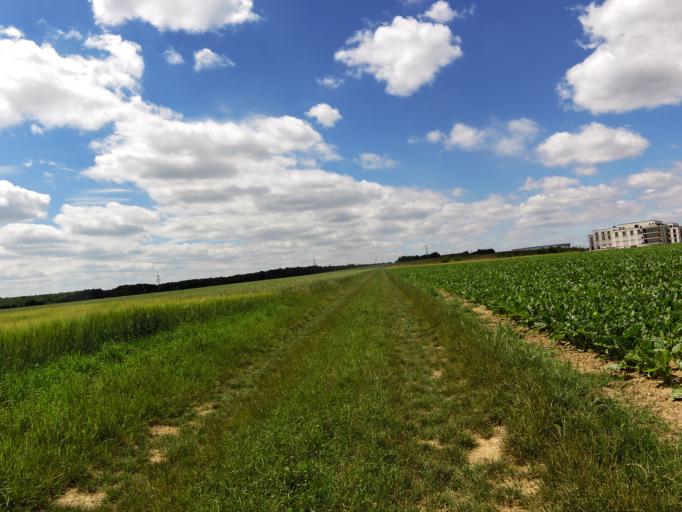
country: DE
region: Bavaria
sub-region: Regierungsbezirk Unterfranken
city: Kist
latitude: 49.7380
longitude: 9.8478
